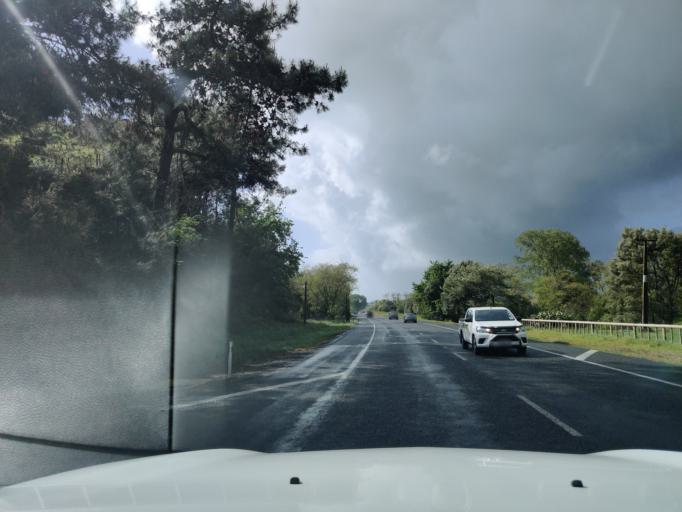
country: NZ
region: Waikato
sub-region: Waipa District
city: Cambridge
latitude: -37.9232
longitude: 175.5626
